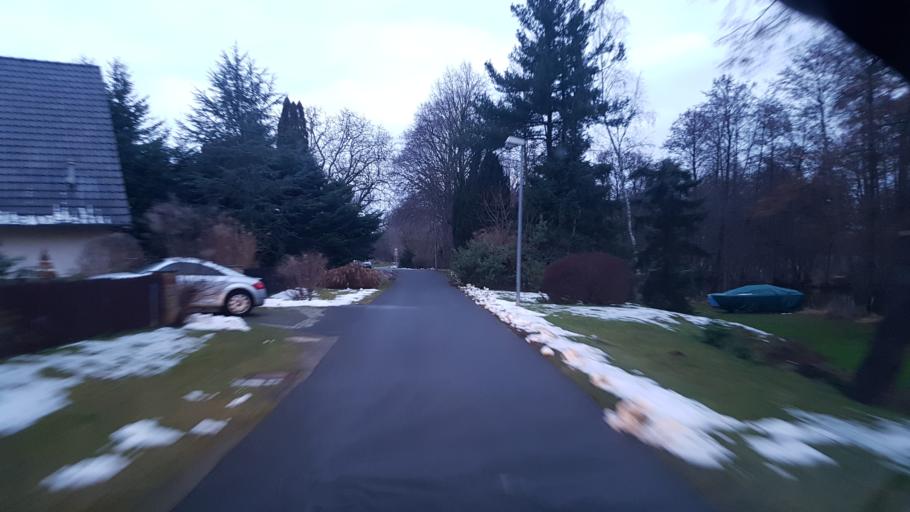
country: DE
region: Brandenburg
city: Tauche
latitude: 52.0870
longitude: 14.1589
